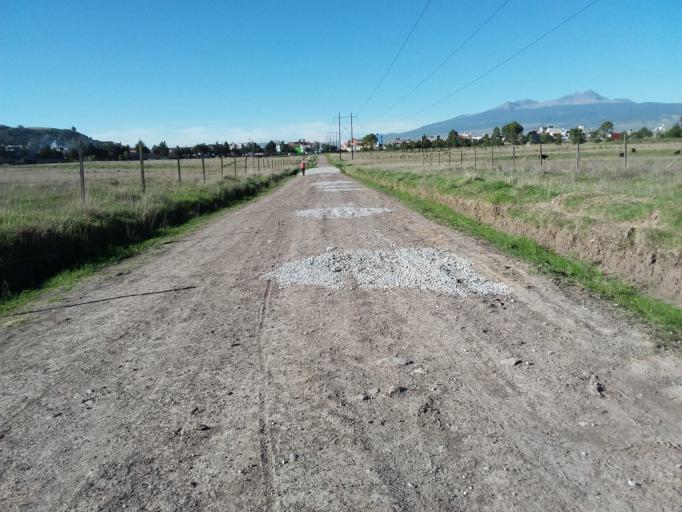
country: MX
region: Mexico
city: San Marcos Yachihuacaltepec
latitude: 19.3091
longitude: -99.6955
